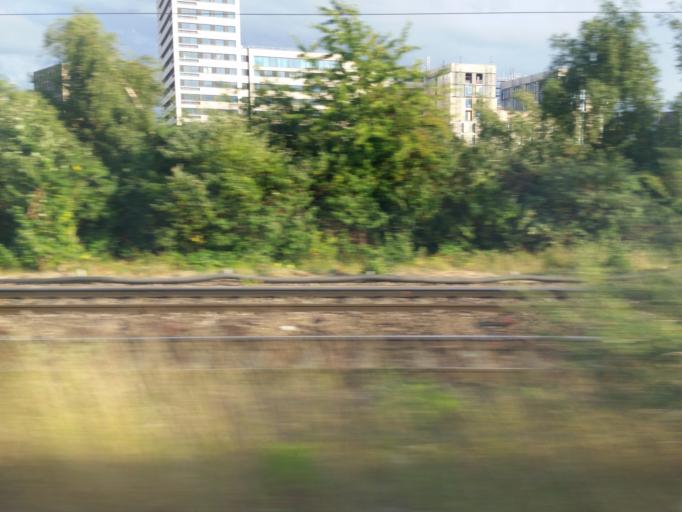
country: GB
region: England
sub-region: Greater London
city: Barnsbury
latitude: 51.5411
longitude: -0.1261
